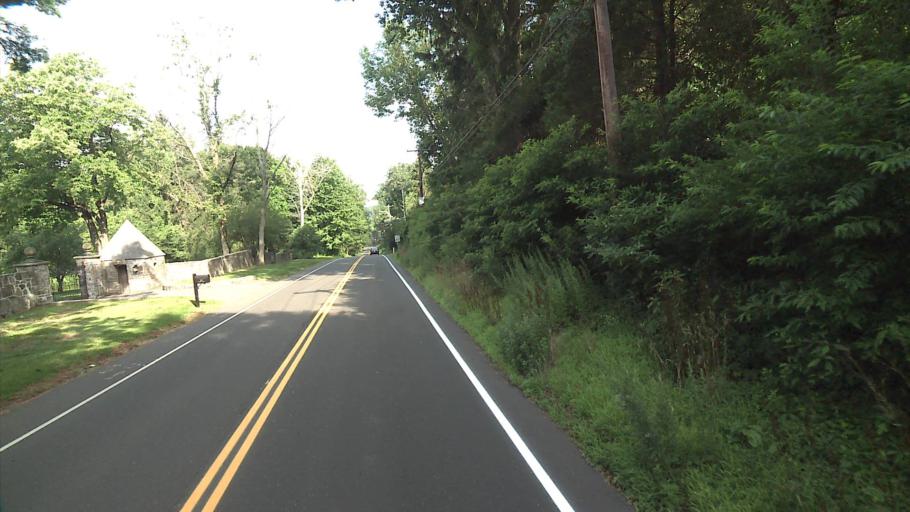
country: US
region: Connecticut
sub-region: New Haven County
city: Woodbridge
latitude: 41.3434
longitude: -73.0154
